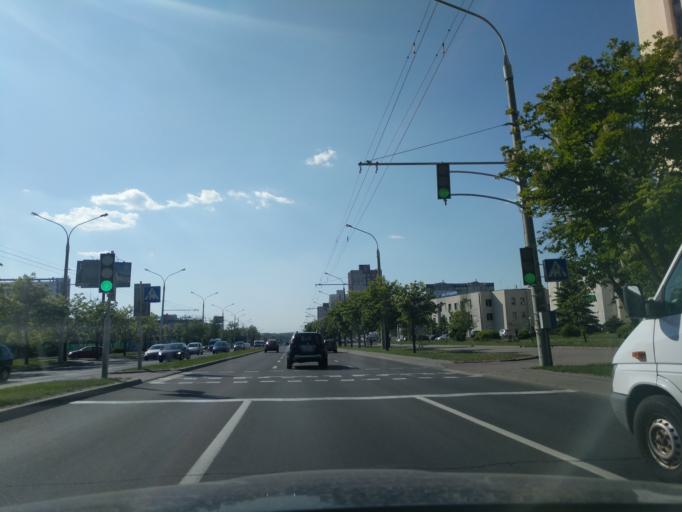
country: BY
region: Minsk
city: Minsk
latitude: 53.9274
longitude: 27.5901
